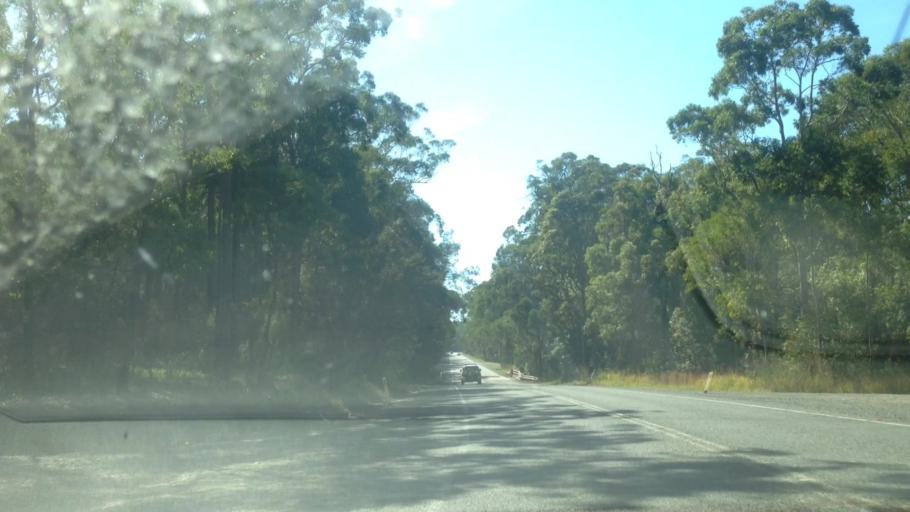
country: AU
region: New South Wales
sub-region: Lake Macquarie Shire
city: Toronto
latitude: -32.9878
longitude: 151.5060
